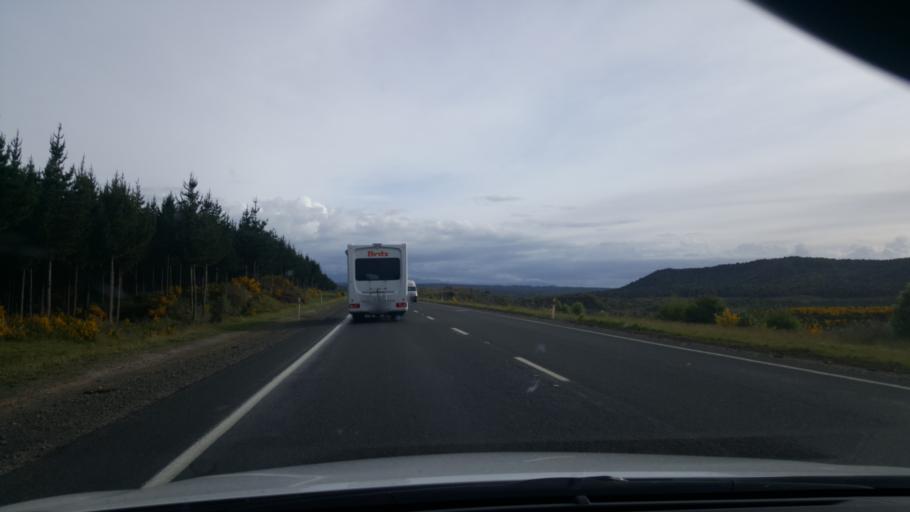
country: NZ
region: Waikato
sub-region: Taupo District
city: Taupo
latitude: -38.8303
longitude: 176.0661
